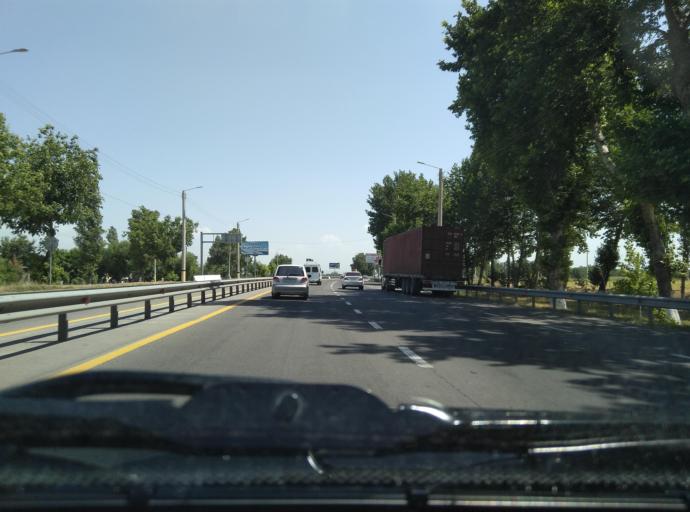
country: UZ
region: Toshkent Shahri
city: Bektemir
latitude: 41.2419
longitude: 69.3995
